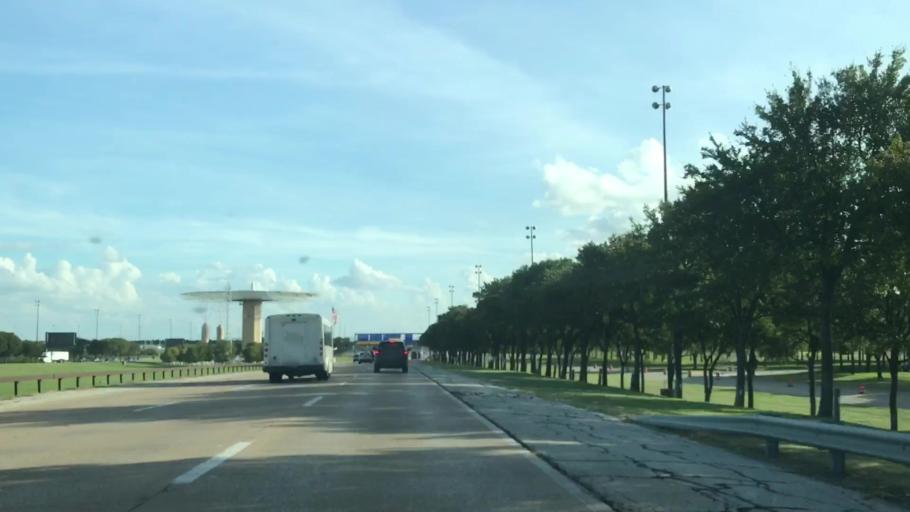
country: US
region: Texas
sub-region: Tarrant County
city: Euless
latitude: 32.8729
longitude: -97.0412
